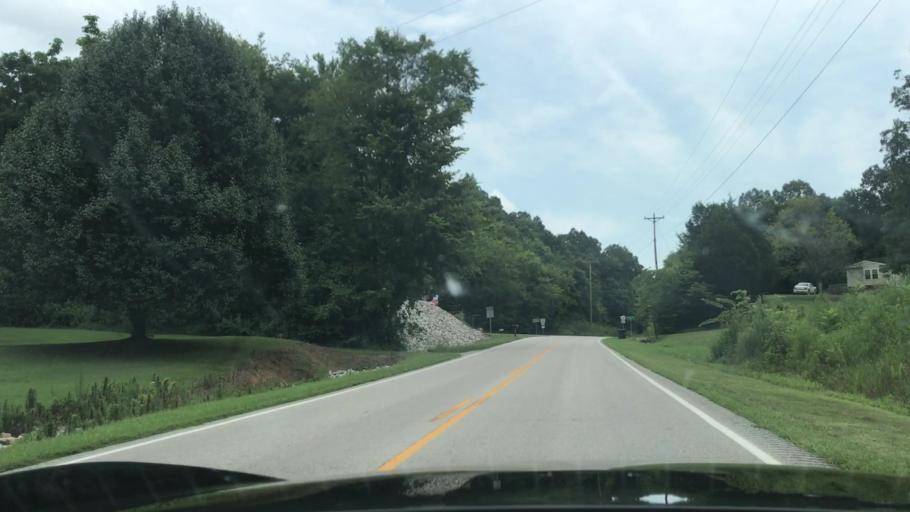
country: US
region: Kentucky
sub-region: Ohio County
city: Oak Grove
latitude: 37.2071
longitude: -86.8920
